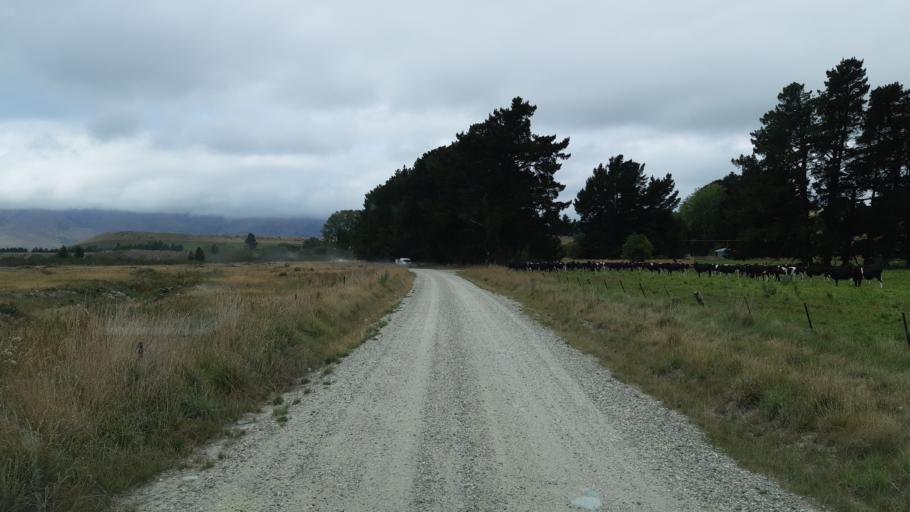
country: NZ
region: Otago
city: Oamaru
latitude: -44.8151
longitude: 170.5168
